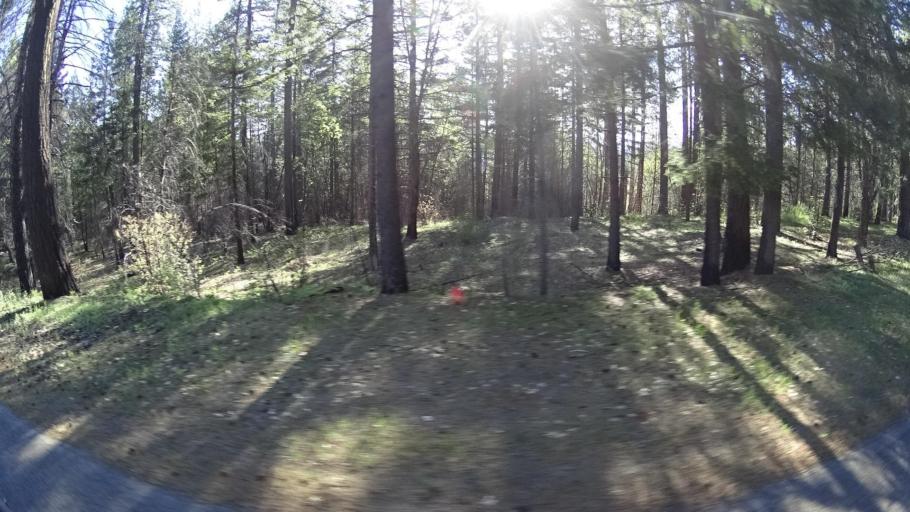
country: US
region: California
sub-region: Lake County
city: Upper Lake
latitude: 39.3057
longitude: -122.9357
